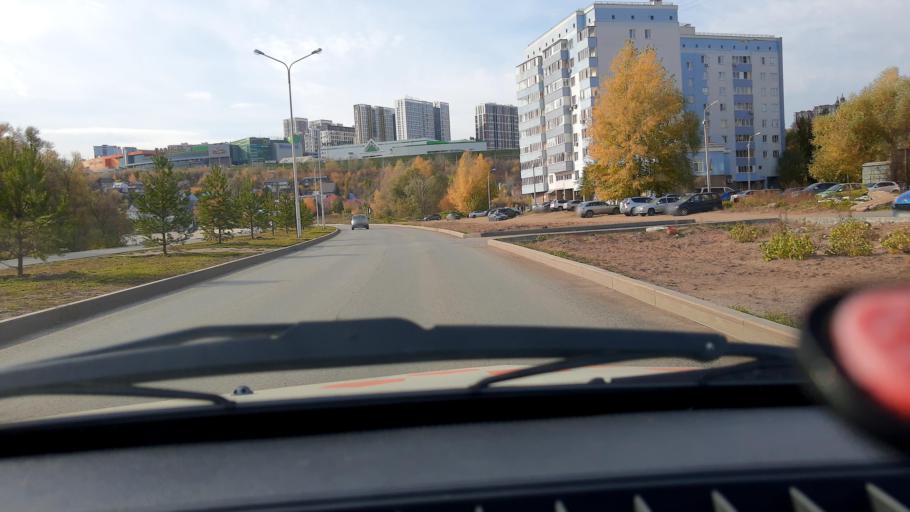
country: RU
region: Bashkortostan
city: Ufa
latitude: 54.7602
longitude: 56.0515
